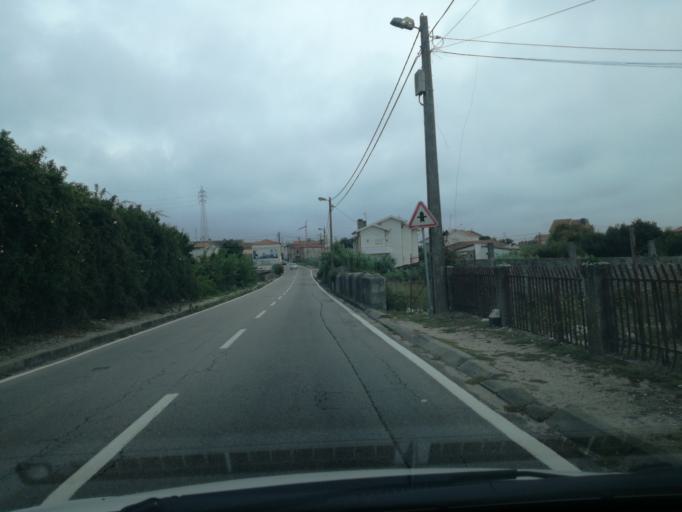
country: PT
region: Aveiro
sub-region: Espinho
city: Espinho
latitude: 40.9986
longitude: -8.6364
